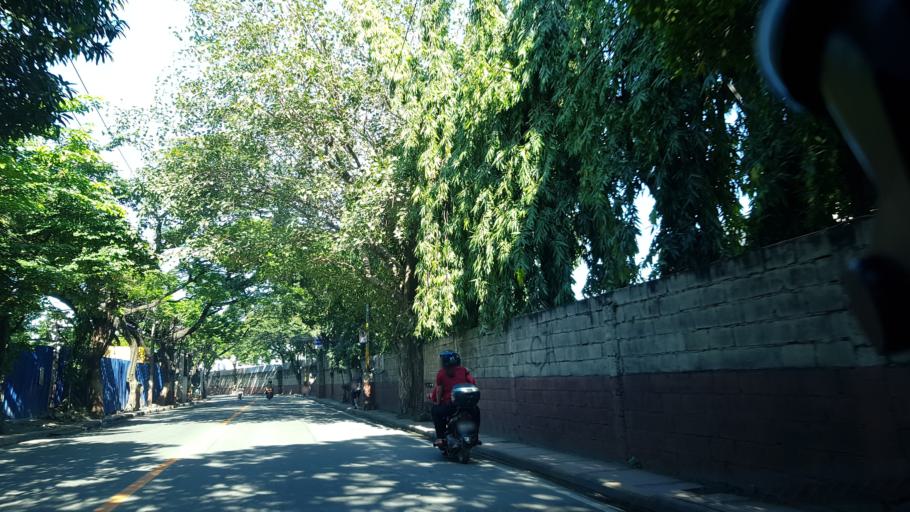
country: PH
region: Metro Manila
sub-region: Pasig
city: Pasig City
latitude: 14.5755
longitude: 121.0892
